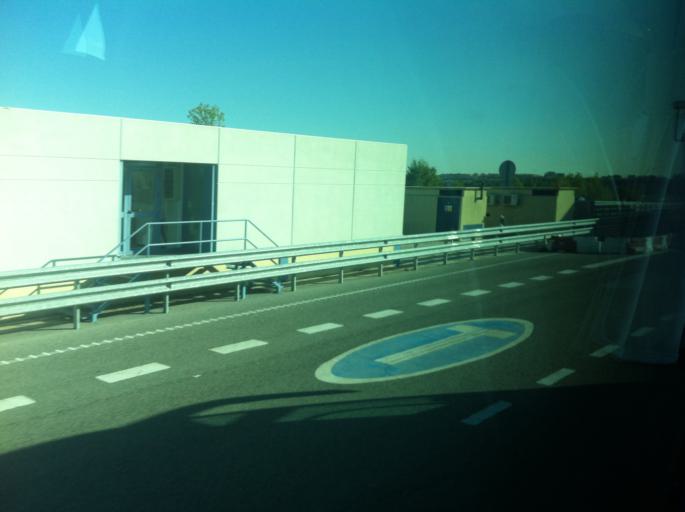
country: ES
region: Madrid
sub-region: Provincia de Madrid
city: Barajas de Madrid
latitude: 40.4751
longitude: -3.6017
